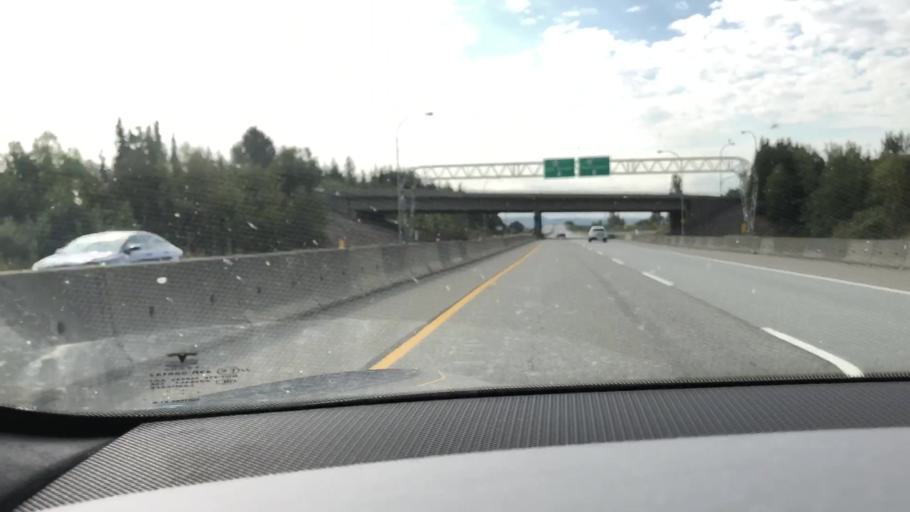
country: CA
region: British Columbia
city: Delta
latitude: 49.1037
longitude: -122.9012
